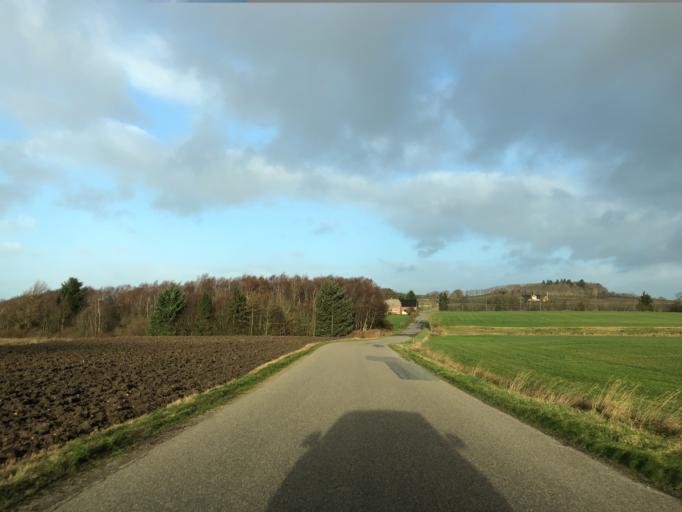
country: DK
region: Central Jutland
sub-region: Ringkobing-Skjern Kommune
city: Videbaek
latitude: 56.1806
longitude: 8.5393
